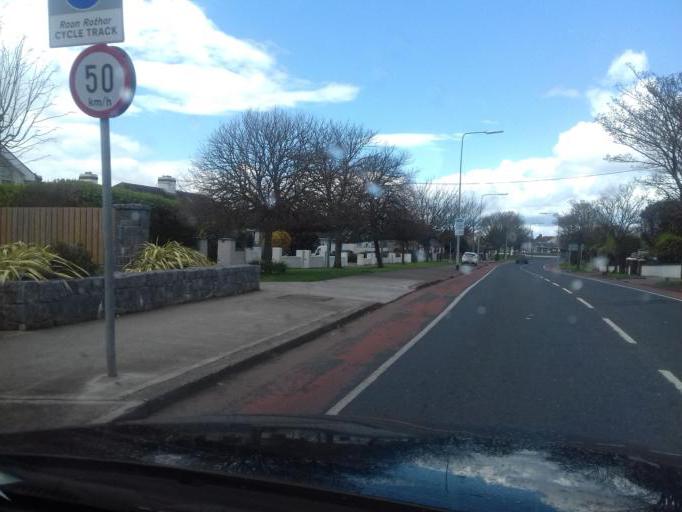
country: IE
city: Bayside
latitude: 53.3852
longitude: -6.1436
